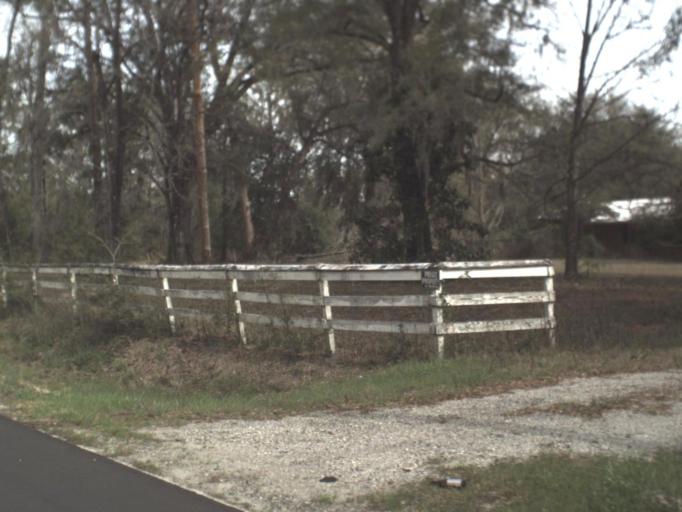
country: US
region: Florida
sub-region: Gadsden County
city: Midway
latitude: 30.4249
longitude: -84.5370
